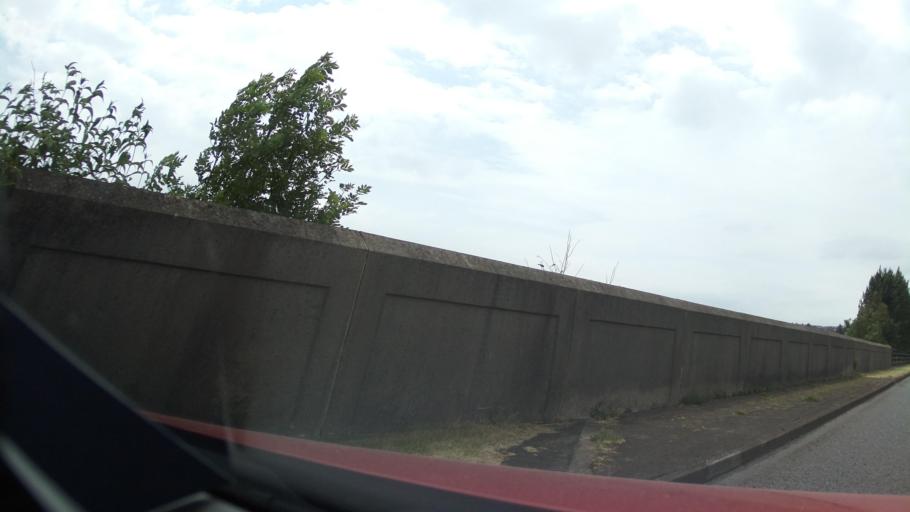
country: GB
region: Wales
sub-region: Vale of Glamorgan
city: Barry
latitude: 51.4043
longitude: -3.2587
